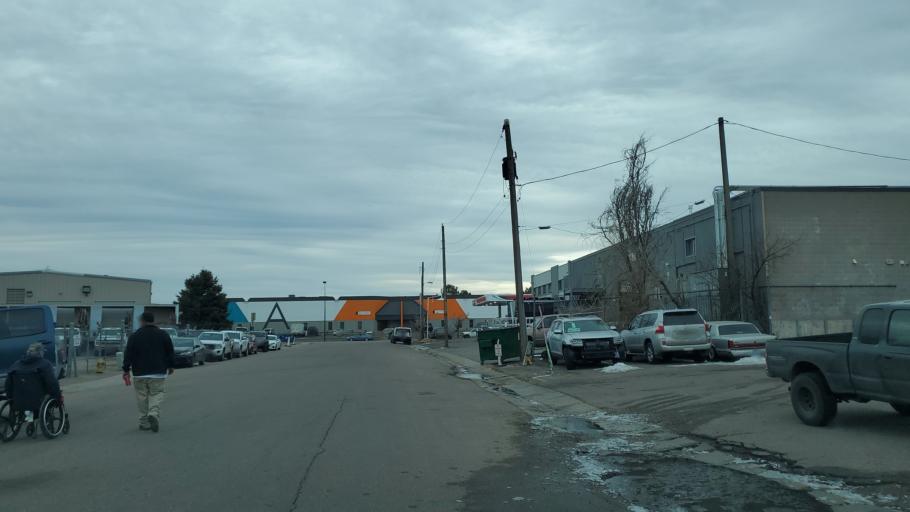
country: US
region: Colorado
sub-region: Denver County
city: Denver
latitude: 39.6978
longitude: -104.9945
